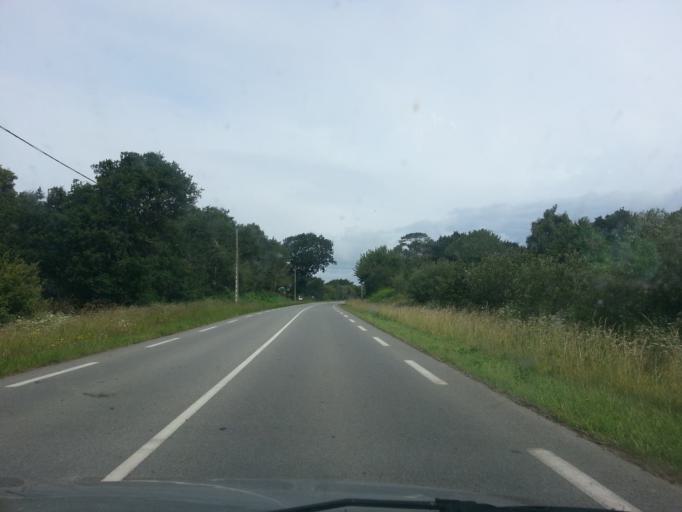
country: FR
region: Brittany
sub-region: Departement du Morbihan
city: Merlevenez
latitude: 47.7170
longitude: -3.2265
